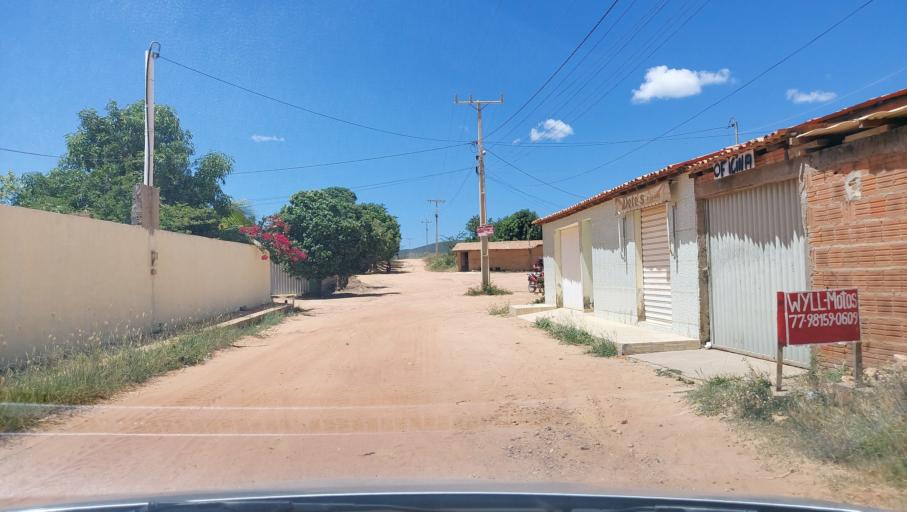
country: BR
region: Bahia
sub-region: Oliveira Dos Brejinhos
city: Beira Rio
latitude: -12.0022
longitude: -42.6294
